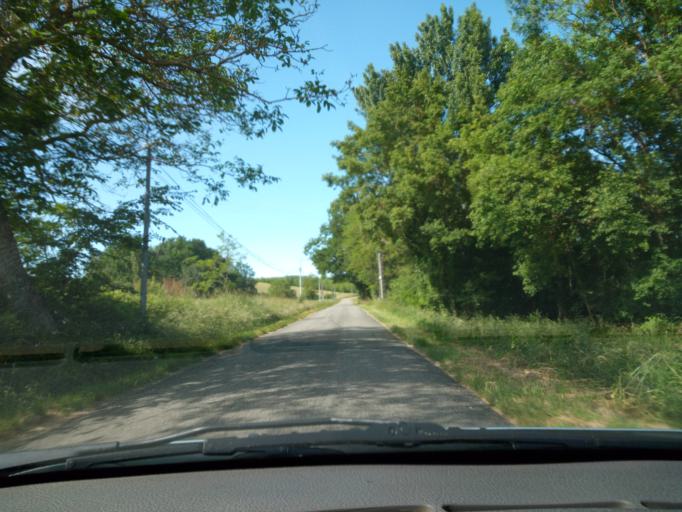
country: FR
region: Midi-Pyrenees
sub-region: Departement du Tarn-et-Garonne
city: Molieres
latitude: 44.2300
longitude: 1.3292
